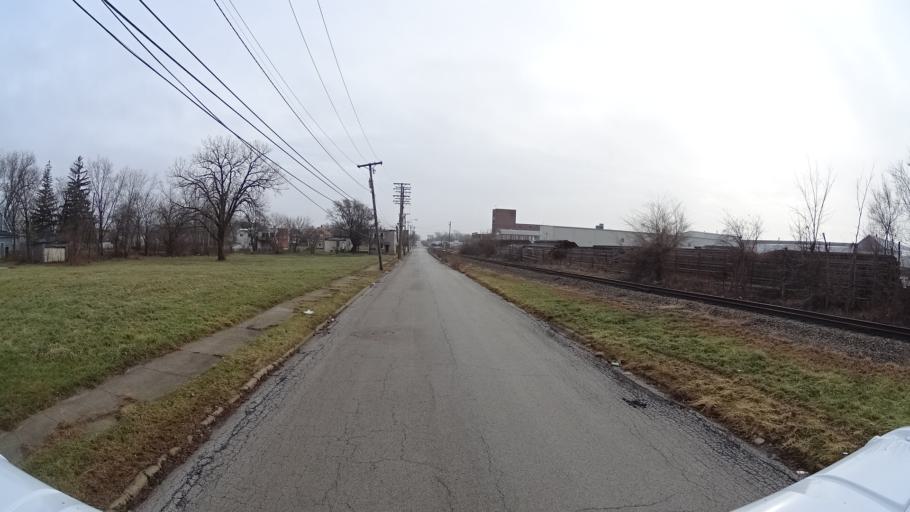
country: US
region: Illinois
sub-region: Cook County
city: Chicago Heights
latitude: 41.5013
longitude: -87.6297
